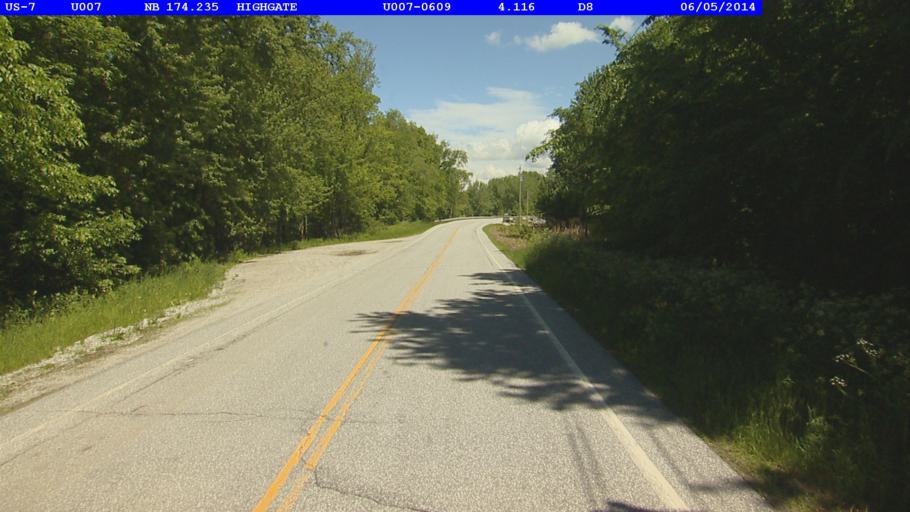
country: US
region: Vermont
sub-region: Franklin County
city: Swanton
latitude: 44.9870
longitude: -73.0893
